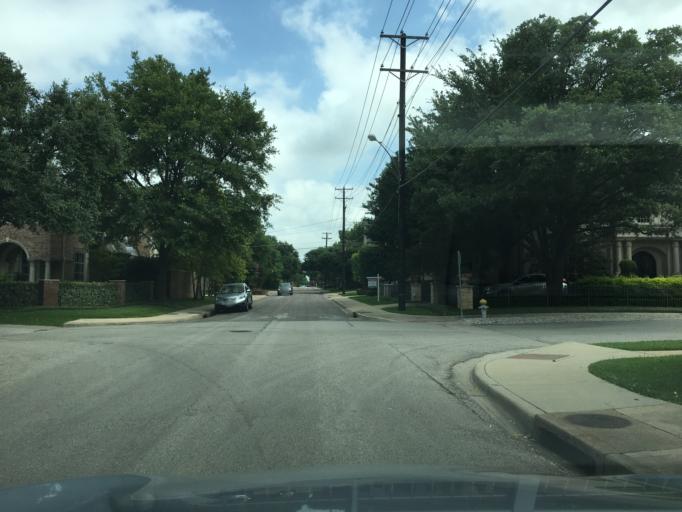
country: US
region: Texas
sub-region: Dallas County
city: University Park
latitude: 32.8840
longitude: -96.7932
